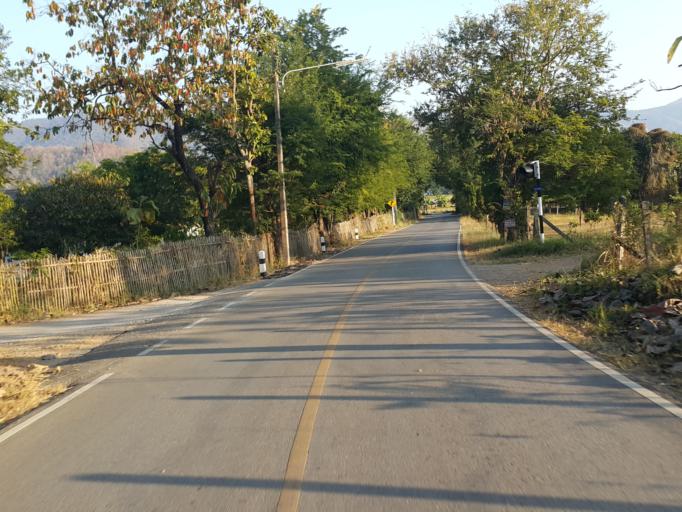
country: TH
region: Chiang Mai
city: Mae On
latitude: 18.7936
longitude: 99.2538
